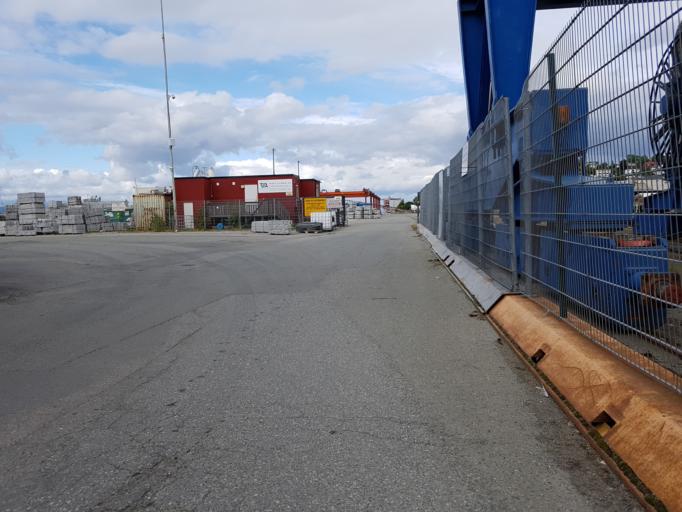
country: NO
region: Sor-Trondelag
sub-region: Trondheim
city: Trondheim
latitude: 63.4414
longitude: 10.4166
